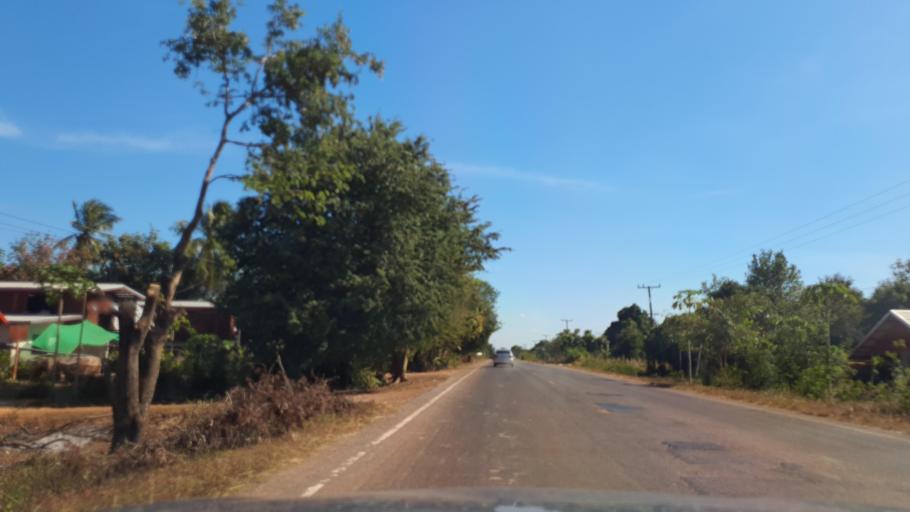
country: TH
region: Kalasin
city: Khao Wong
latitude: 16.7887
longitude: 104.1449
